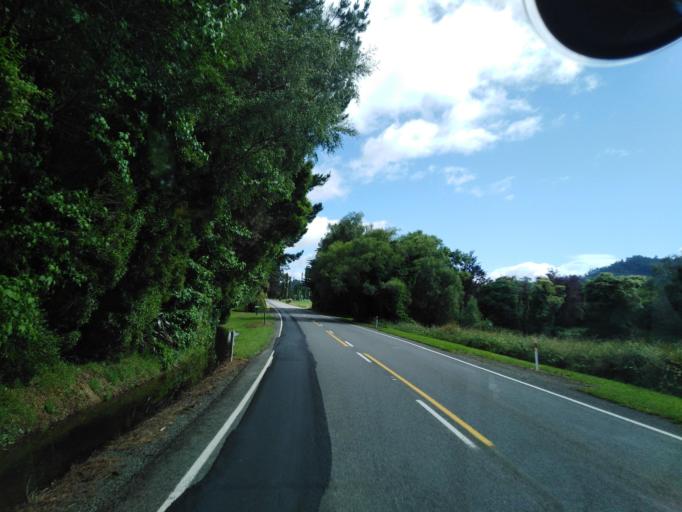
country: NZ
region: Nelson
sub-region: Nelson City
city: Nelson
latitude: -41.2801
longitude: 173.5735
